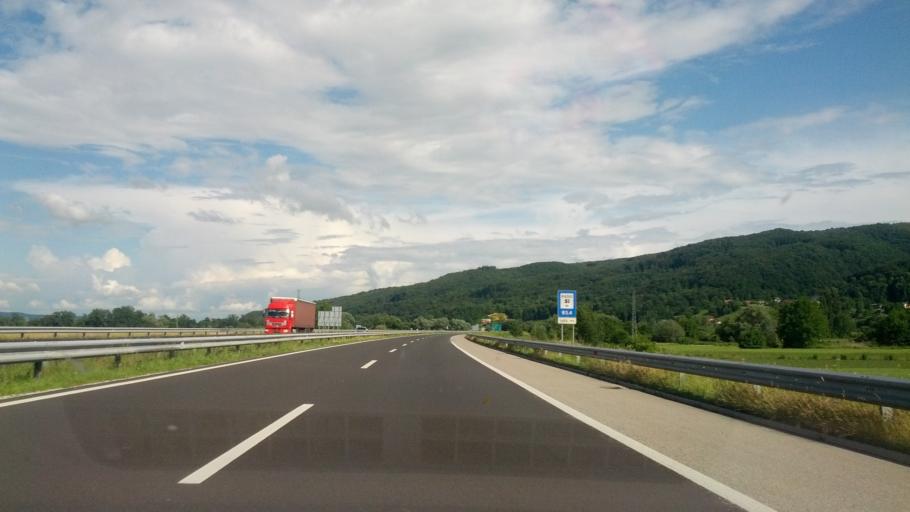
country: SI
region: Brezice
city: Brezice
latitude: 45.8879
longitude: 15.6137
